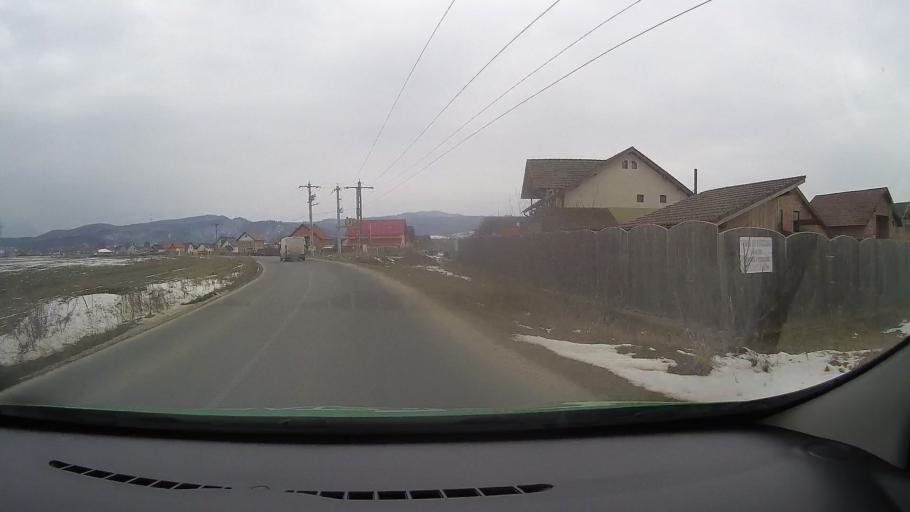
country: RO
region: Brasov
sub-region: Comuna Vulcan
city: Vulcan
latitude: 45.6366
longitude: 25.4338
